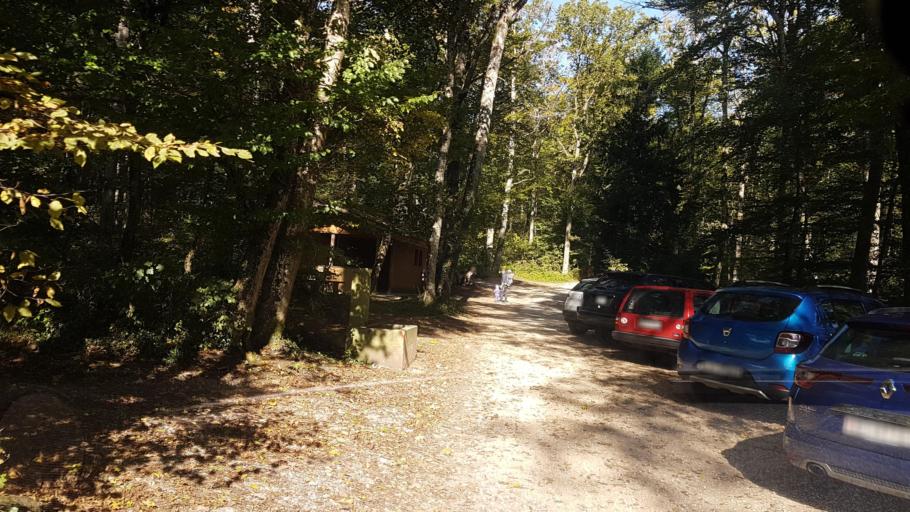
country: CH
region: Aargau
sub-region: Bezirk Laufenburg
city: Sulz
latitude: 47.5184
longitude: 8.1235
